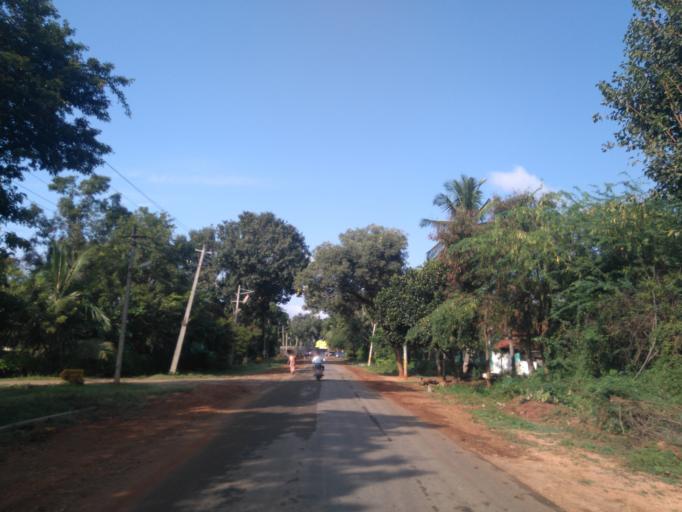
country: IN
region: Karnataka
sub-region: Mysore
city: Tirumakudal Narsipur
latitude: 12.2593
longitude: 77.0140
